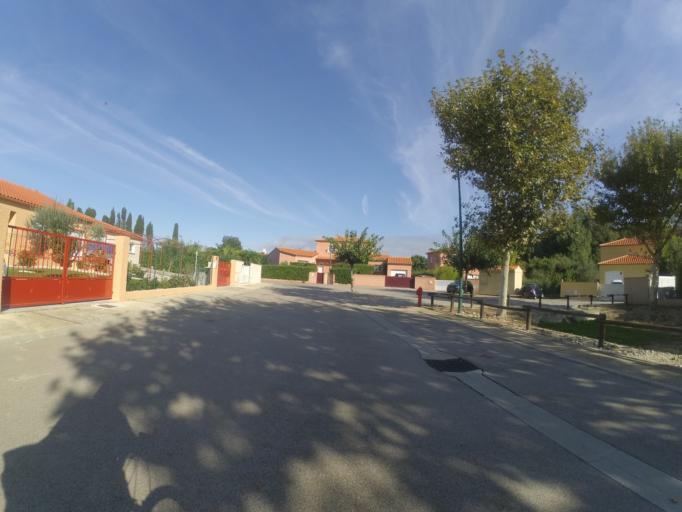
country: FR
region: Languedoc-Roussillon
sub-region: Departement des Pyrenees-Orientales
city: Pezilla-la-Riviere
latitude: 42.6920
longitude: 2.7642
